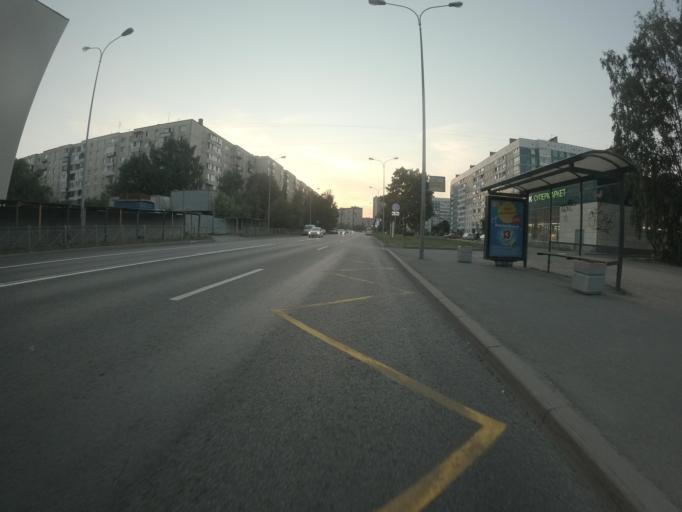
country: RU
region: St.-Petersburg
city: Krasnogvargeisky
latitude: 59.9139
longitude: 30.4593
